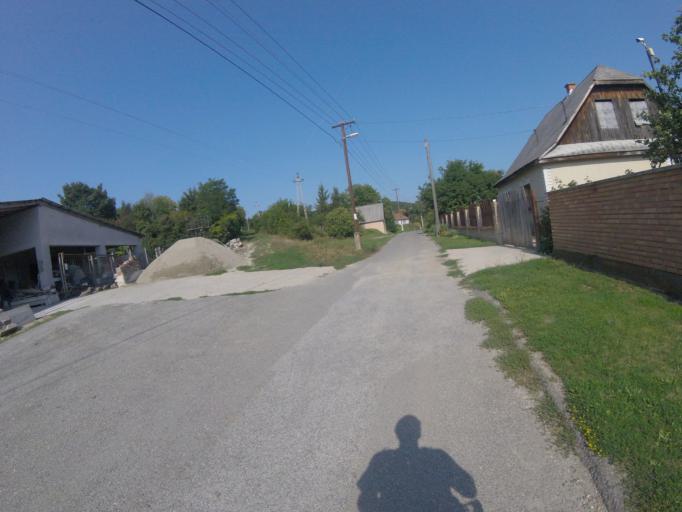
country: HU
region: Nograd
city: Bujak
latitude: 47.8830
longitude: 19.5369
